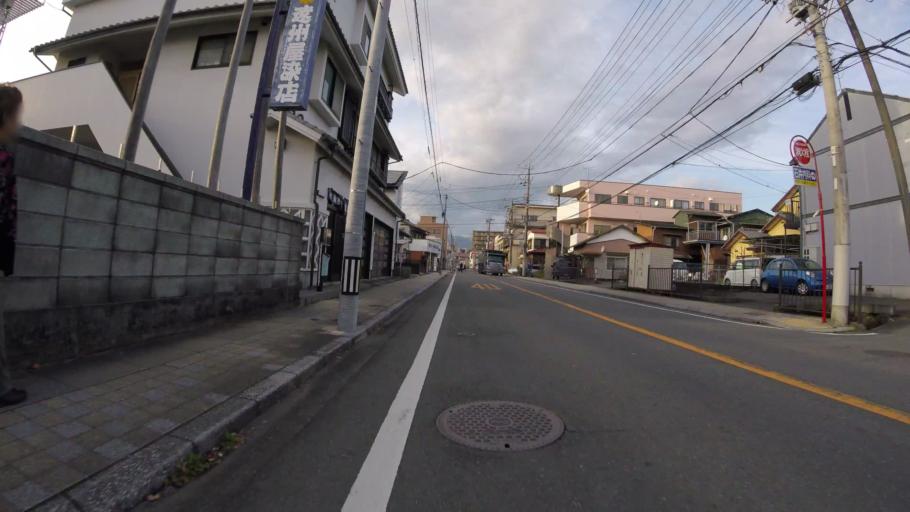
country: JP
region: Shizuoka
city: Mishima
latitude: 35.1145
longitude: 138.9233
